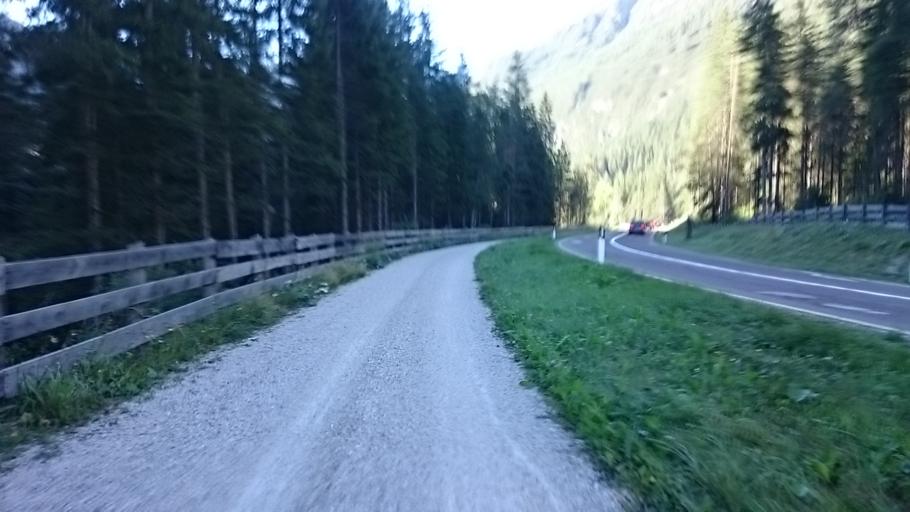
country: IT
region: Trentino-Alto Adige
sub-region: Bolzano
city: Dobbiaco
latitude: 46.6586
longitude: 12.2259
